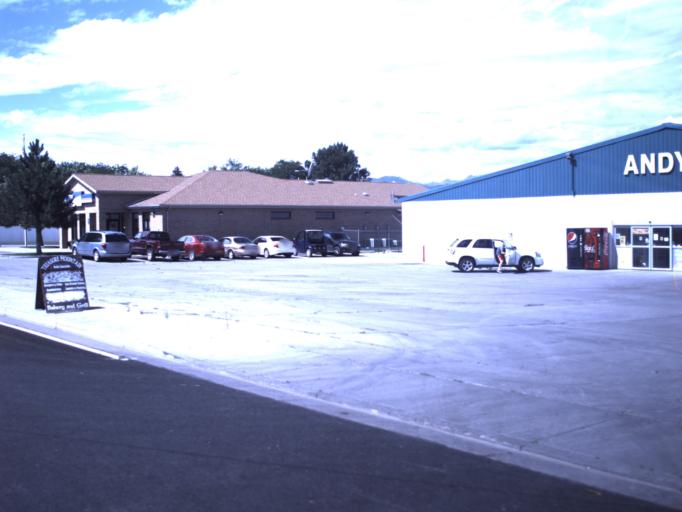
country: US
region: Utah
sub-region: Sevier County
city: Monroe
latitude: 38.6411
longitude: -112.1215
